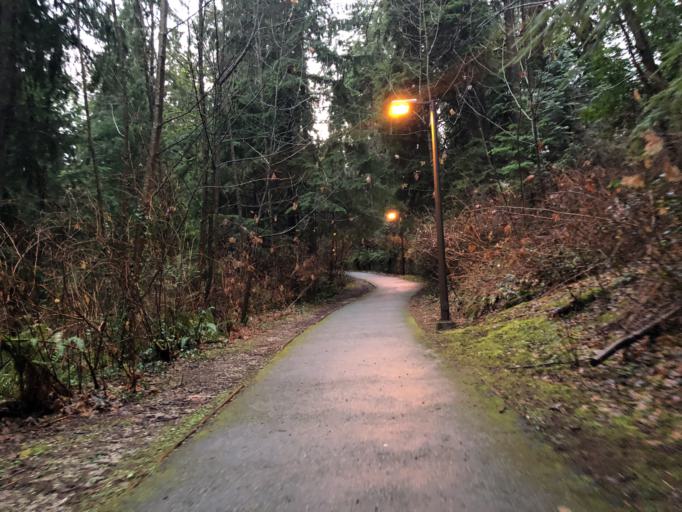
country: CA
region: British Columbia
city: Burnaby
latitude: 49.3226
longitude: -122.9543
